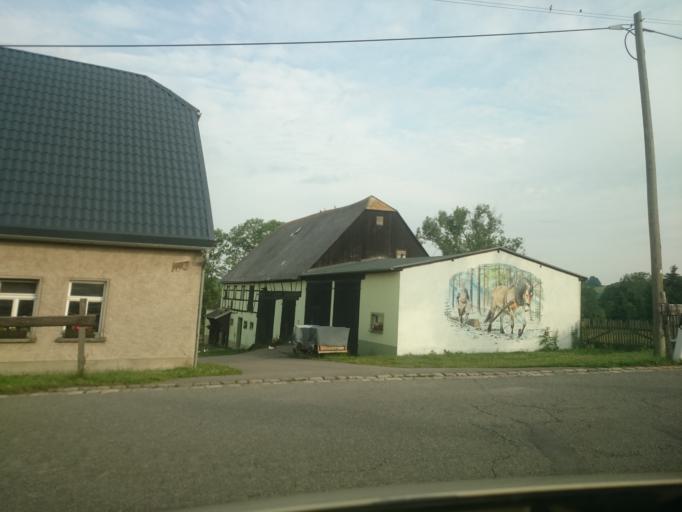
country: DE
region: Saxony
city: Eppendorf
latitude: 50.8400
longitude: 13.2294
